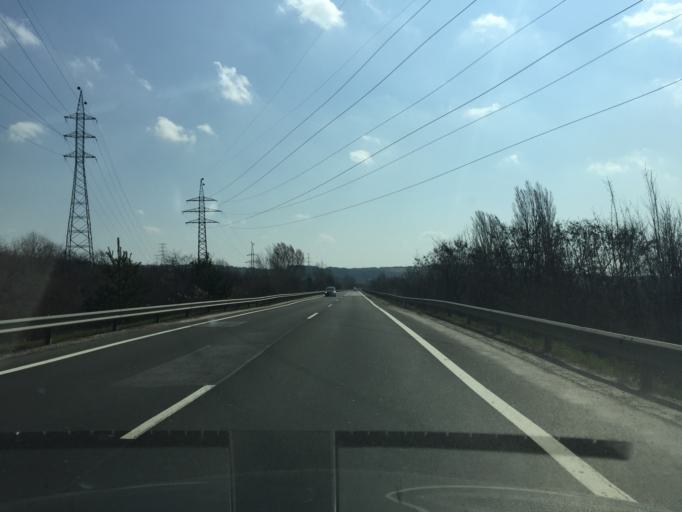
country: HU
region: Pest
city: Vac
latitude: 47.8134
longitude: 19.1090
